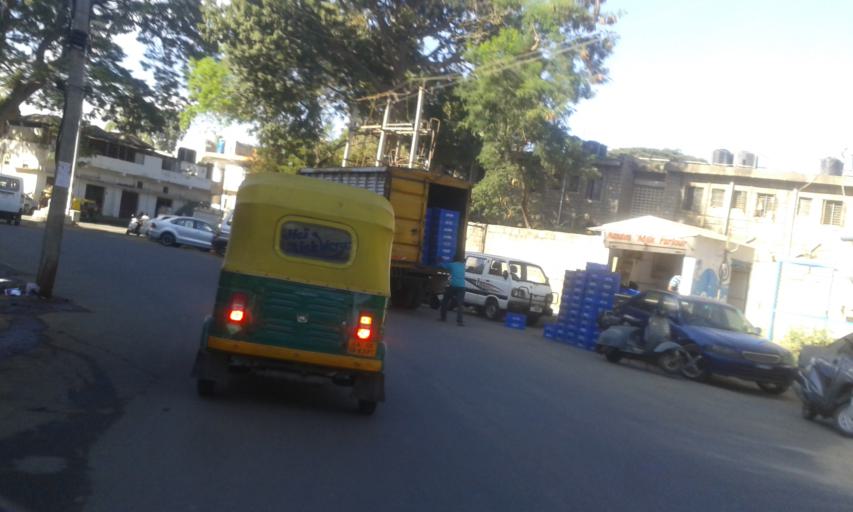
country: IN
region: Karnataka
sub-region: Bangalore Urban
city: Bangalore
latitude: 12.9519
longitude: 77.6081
